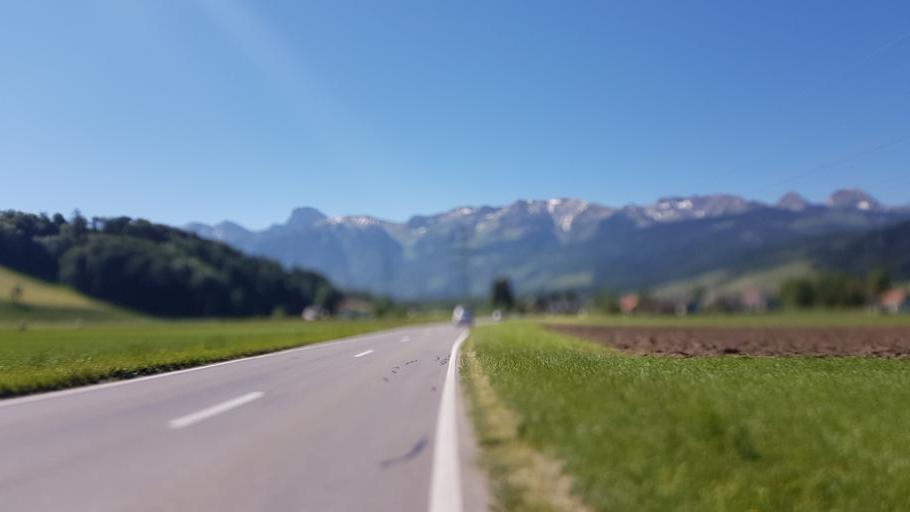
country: CH
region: Bern
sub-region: Thun District
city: Wattenwil
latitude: 46.7762
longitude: 7.5163
